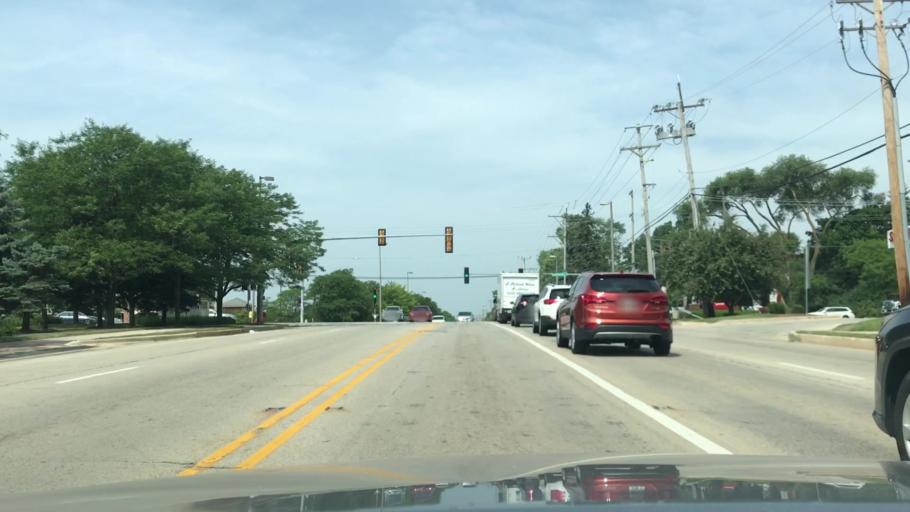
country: US
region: Illinois
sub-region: DuPage County
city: Darien
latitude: 41.7366
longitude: -88.0112
